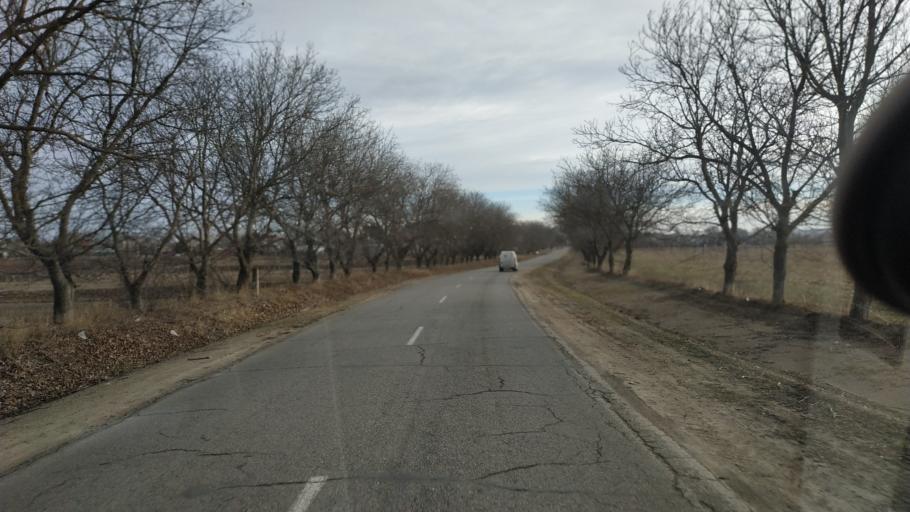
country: MD
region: Criuleni
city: Criuleni
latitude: 47.1575
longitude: 29.1091
